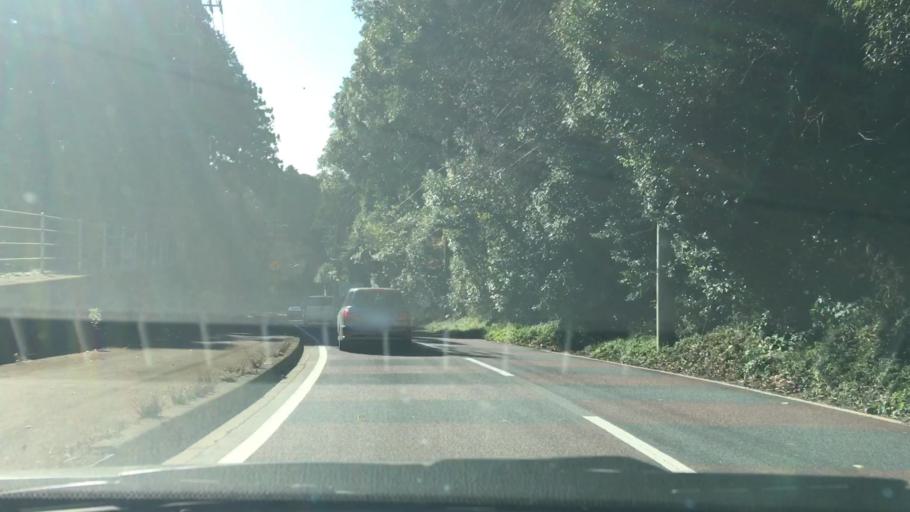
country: JP
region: Chiba
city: Sawara
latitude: 35.8204
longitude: 140.5327
